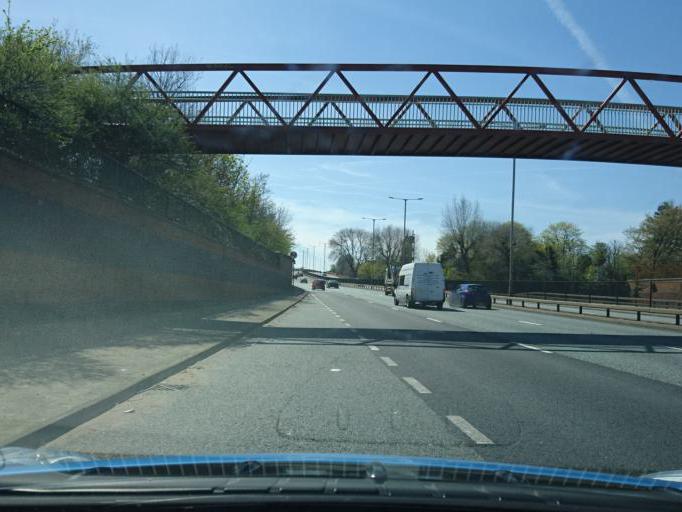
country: GB
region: England
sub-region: Greater London
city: Hendon
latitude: 51.5996
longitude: -0.1760
